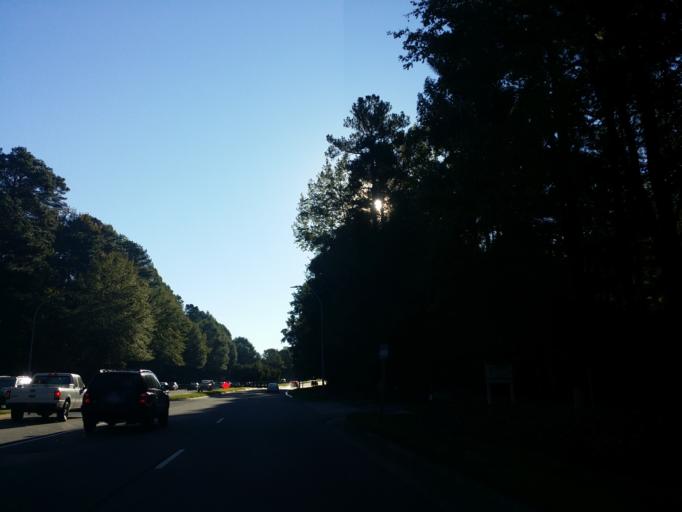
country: US
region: North Carolina
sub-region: Wake County
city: Cary
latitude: 35.8309
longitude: -78.7769
